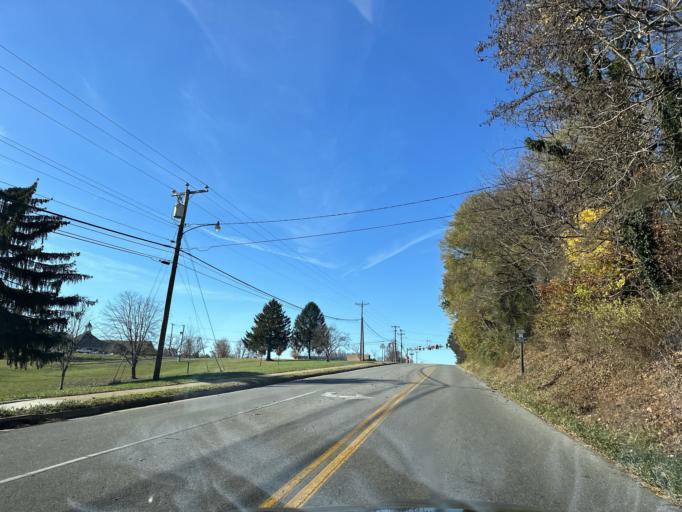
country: US
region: Virginia
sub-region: City of Staunton
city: Staunton
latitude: 38.1659
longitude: -79.0547
